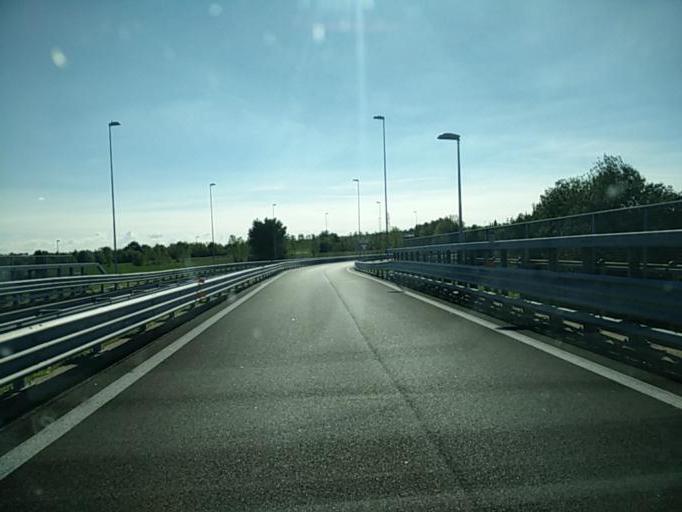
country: IT
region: Lombardy
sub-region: Provincia di Brescia
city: San Martino della Battaglia
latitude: 45.4339
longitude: 10.6102
